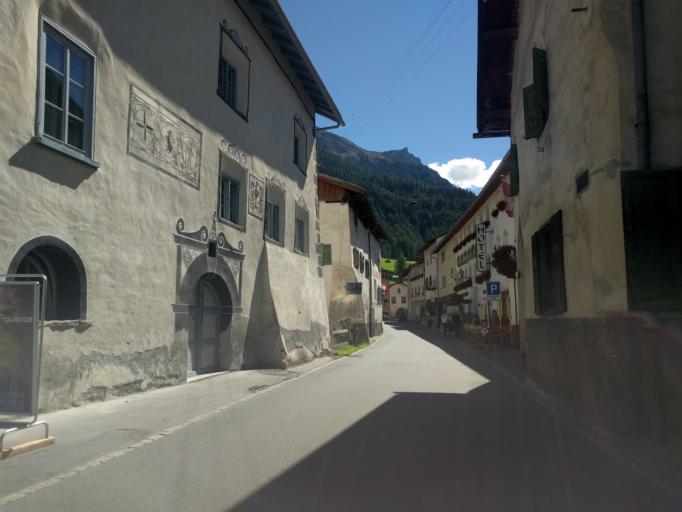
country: IT
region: Trentino-Alto Adige
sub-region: Bolzano
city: Tubre
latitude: 46.6027
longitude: 10.4254
